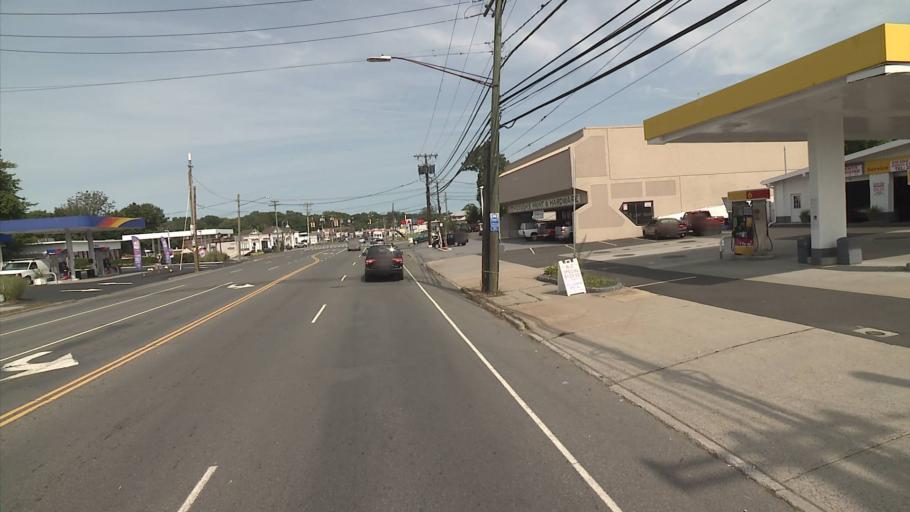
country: US
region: Connecticut
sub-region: Fairfield County
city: North Stamford
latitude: 41.1021
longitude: -73.5479
